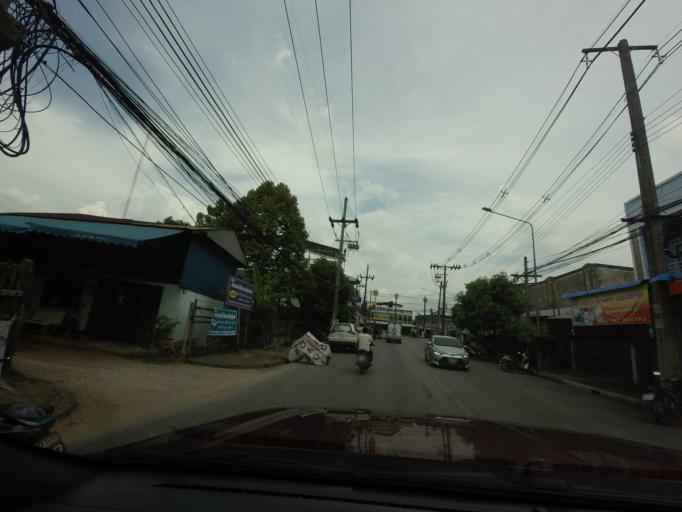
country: TH
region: Yala
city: Yala
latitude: 6.5414
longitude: 101.2889
